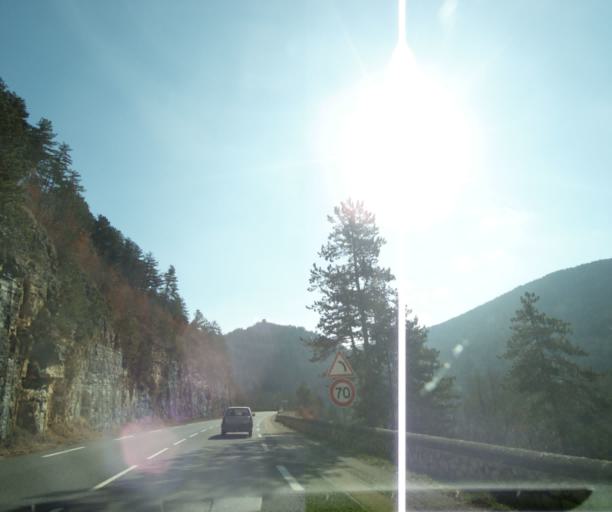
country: FR
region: Languedoc-Roussillon
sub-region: Departement de la Lozere
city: Mende
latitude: 44.4827
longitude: 3.4500
